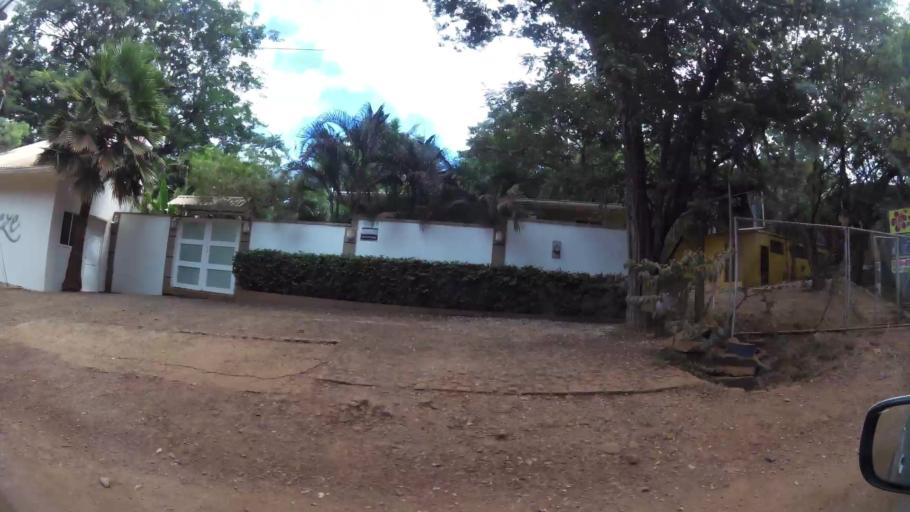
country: CR
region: Guanacaste
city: Santa Cruz
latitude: 10.2961
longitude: -85.8421
